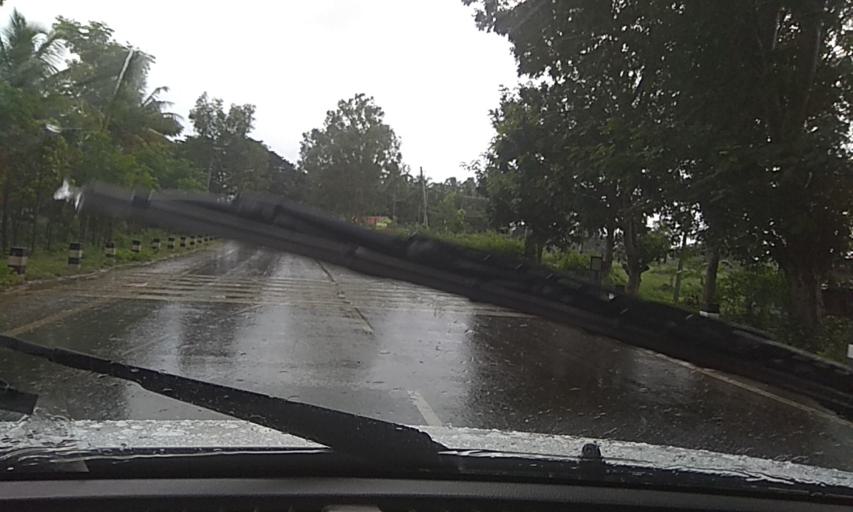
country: IN
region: Karnataka
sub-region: Tumkur
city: Kunigal
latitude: 12.9518
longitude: 77.0276
